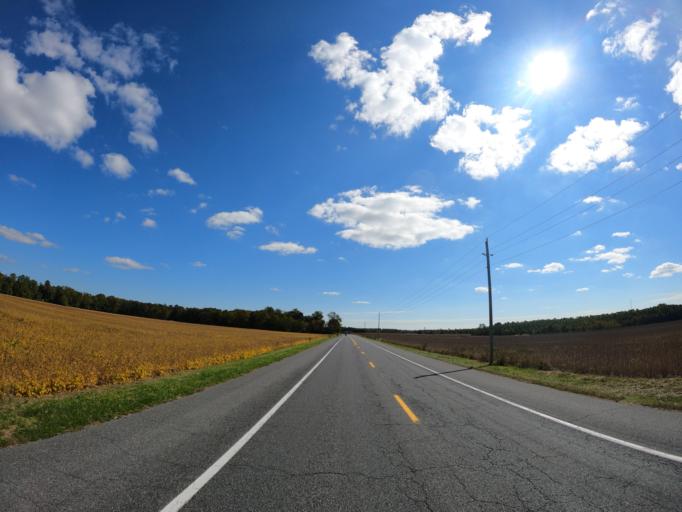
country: US
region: Delaware
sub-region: Sussex County
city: Bridgeville
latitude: 38.8277
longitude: -75.6578
